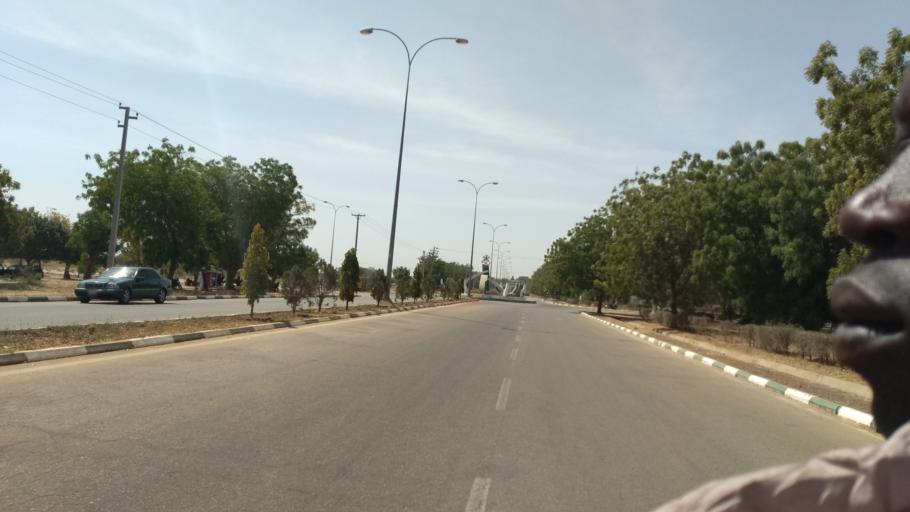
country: NG
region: Jigawa
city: Dutse
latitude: 11.6841
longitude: 9.3342
